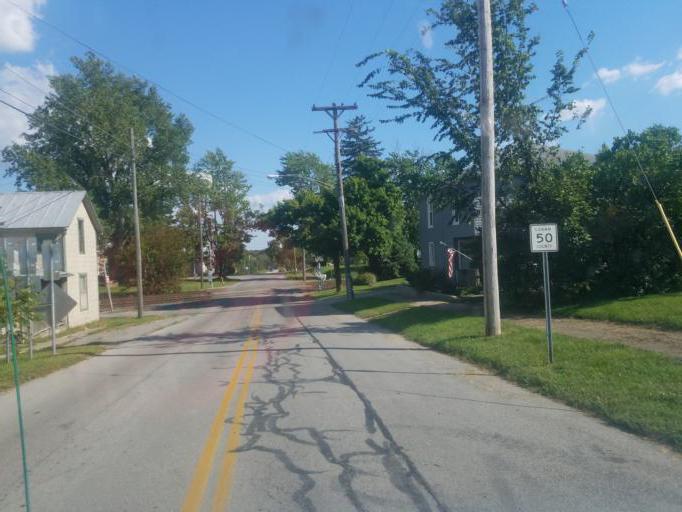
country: US
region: Ohio
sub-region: Shelby County
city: Jackson Center
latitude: 40.4686
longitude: -84.0650
